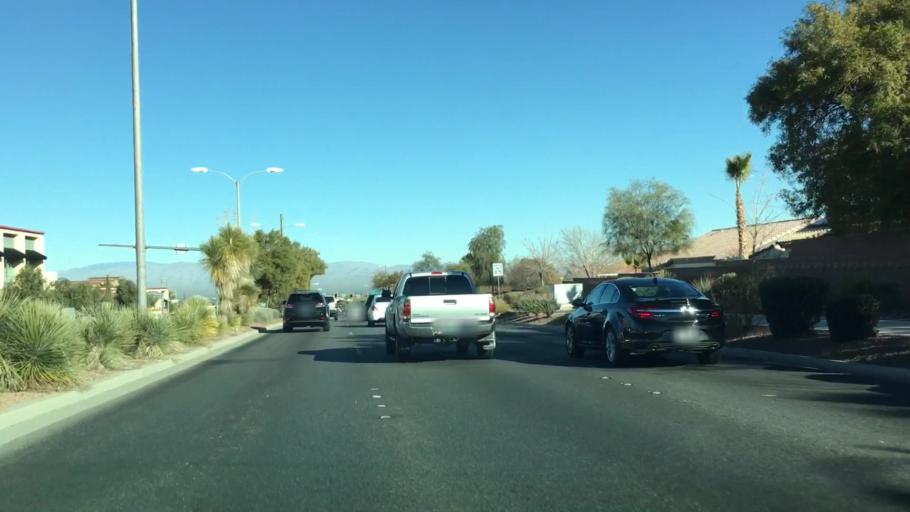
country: US
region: Nevada
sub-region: Clark County
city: Whitney
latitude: 35.9863
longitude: -115.1009
